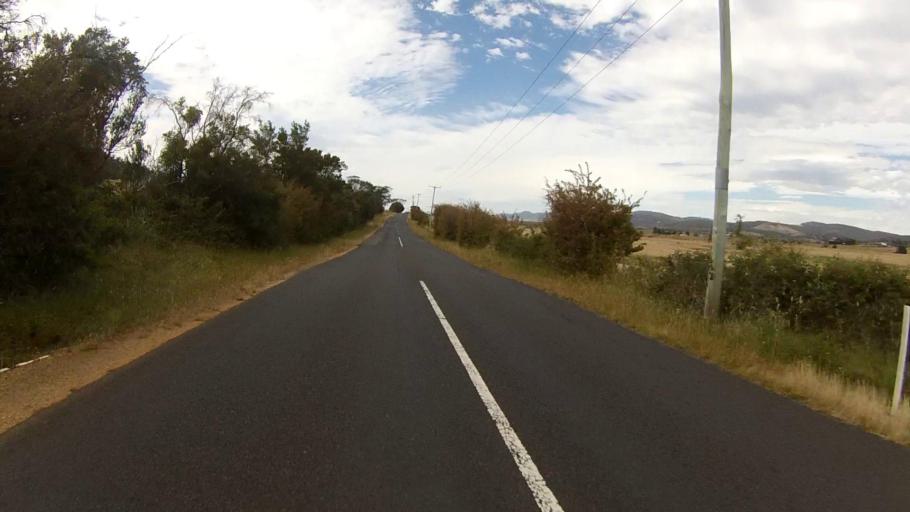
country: AU
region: Tasmania
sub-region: Clarence
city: Cambridge
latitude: -42.7254
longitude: 147.3976
